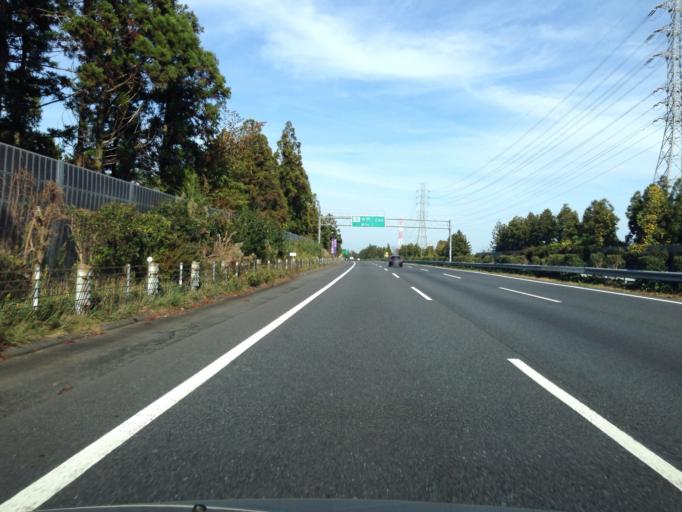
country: JP
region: Ibaraki
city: Mito-shi
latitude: 36.3637
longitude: 140.3789
